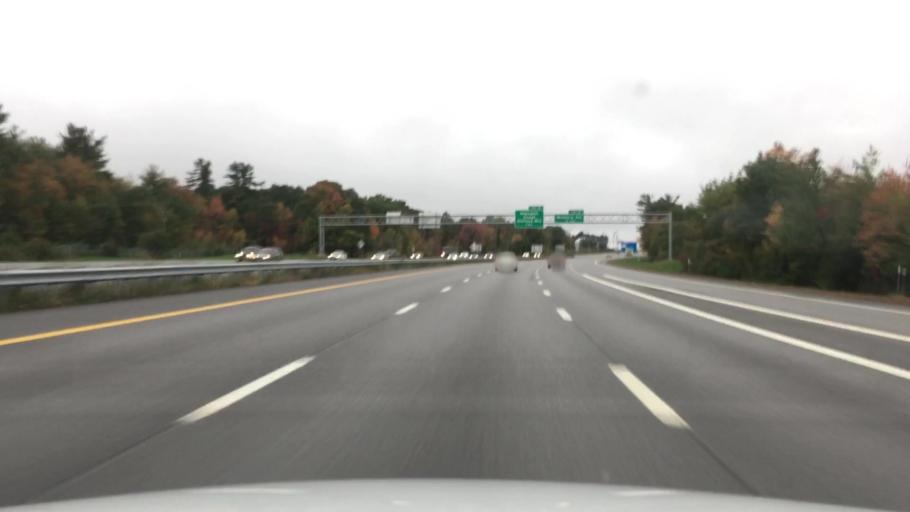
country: US
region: Maine
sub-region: York County
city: South Eliot
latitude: 43.0938
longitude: -70.8061
